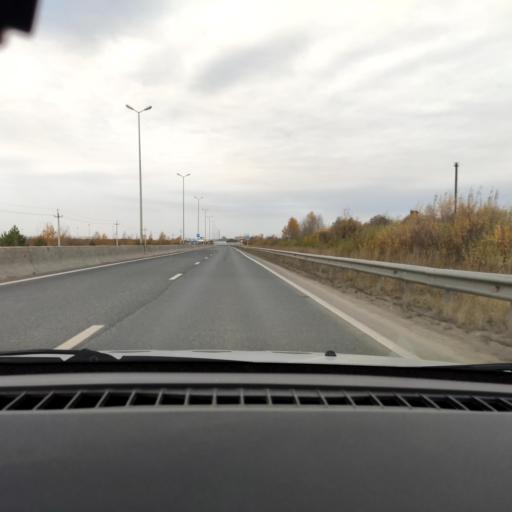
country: RU
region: Perm
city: Kondratovo
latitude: 58.0057
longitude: 56.0653
